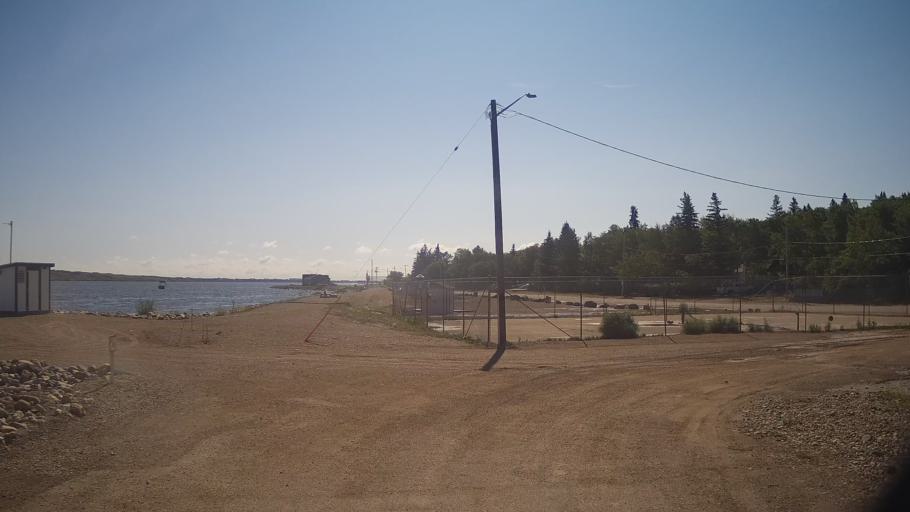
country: CA
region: Saskatchewan
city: Watrous
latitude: 51.7219
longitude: -105.4524
